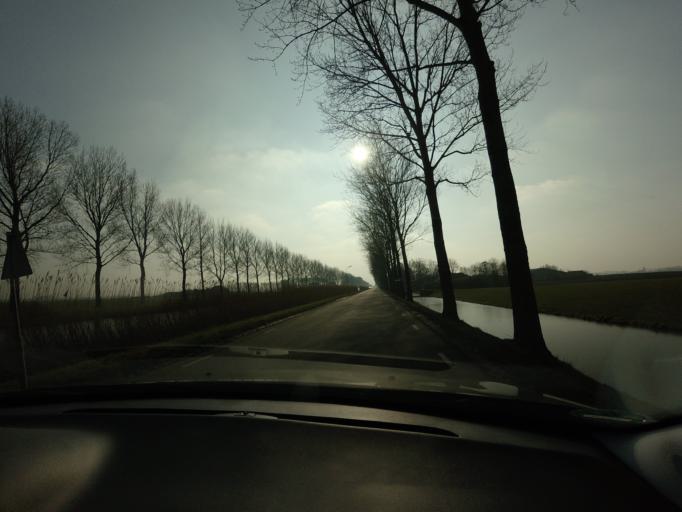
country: NL
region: North Holland
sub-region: Gemeente Alkmaar
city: Alkmaar
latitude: 52.6003
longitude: 4.7879
